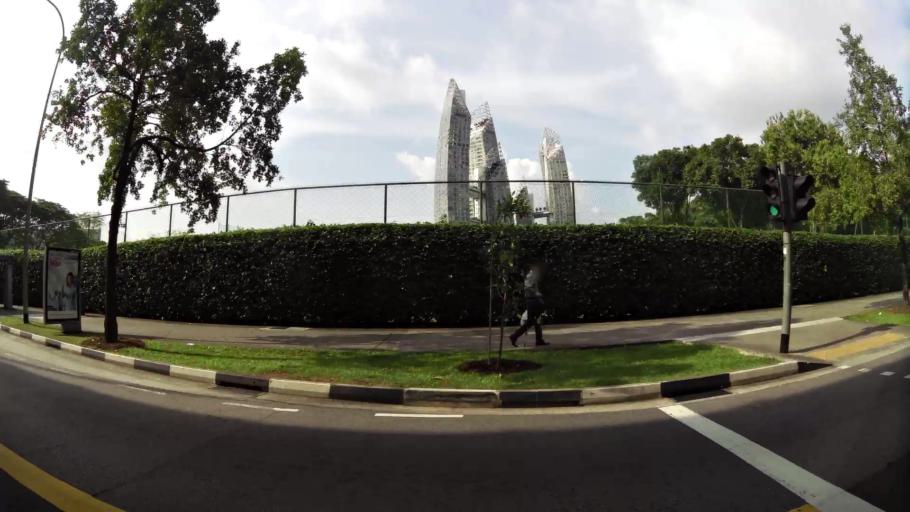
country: SG
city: Singapore
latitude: 1.2699
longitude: 103.8127
